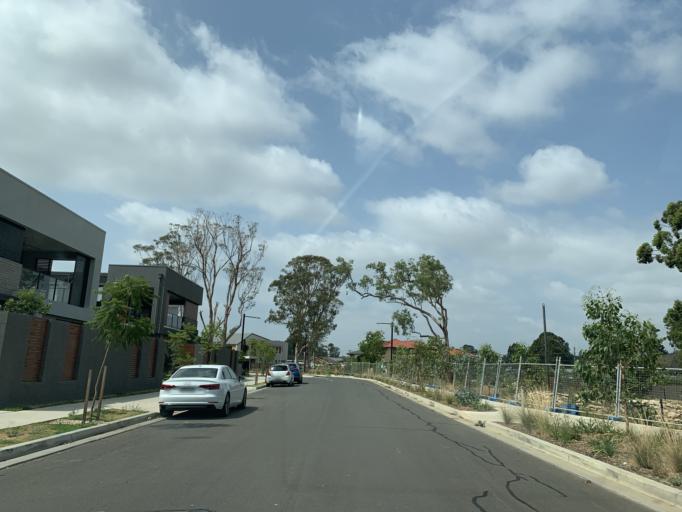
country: AU
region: New South Wales
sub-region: Blacktown
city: Blacktown
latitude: -33.7596
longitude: 150.8994
